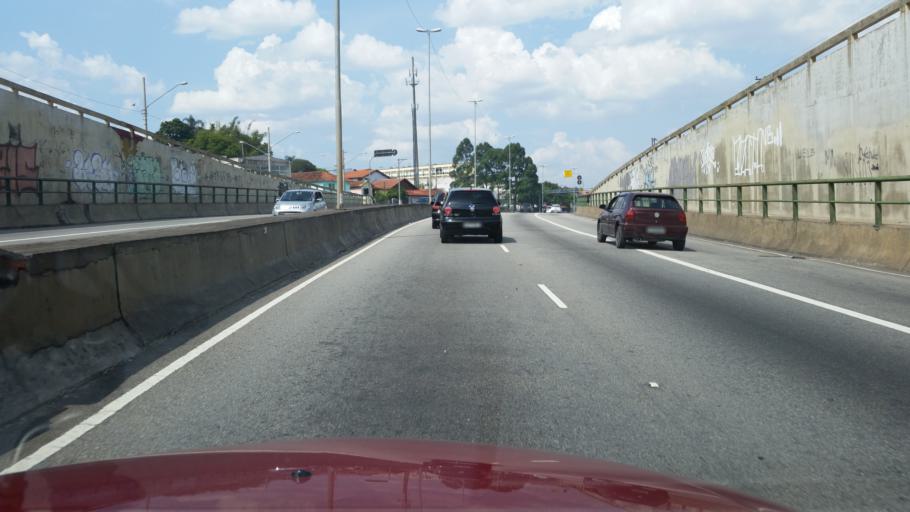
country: BR
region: Sao Paulo
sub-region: Ferraz De Vasconcelos
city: Ferraz de Vasconcelos
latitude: -23.5402
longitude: -46.4639
